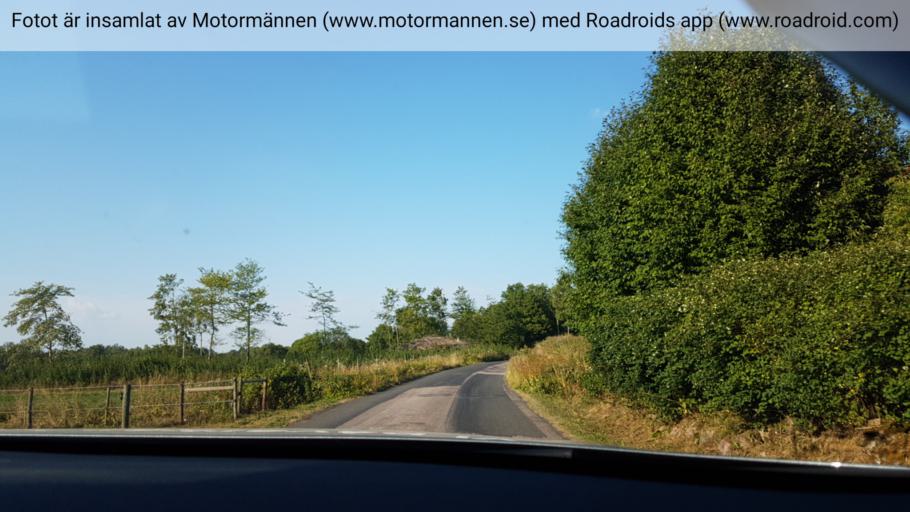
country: SE
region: Vaestra Goetaland
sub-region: Skovde Kommun
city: Skoevde
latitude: 58.4452
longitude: 13.7065
